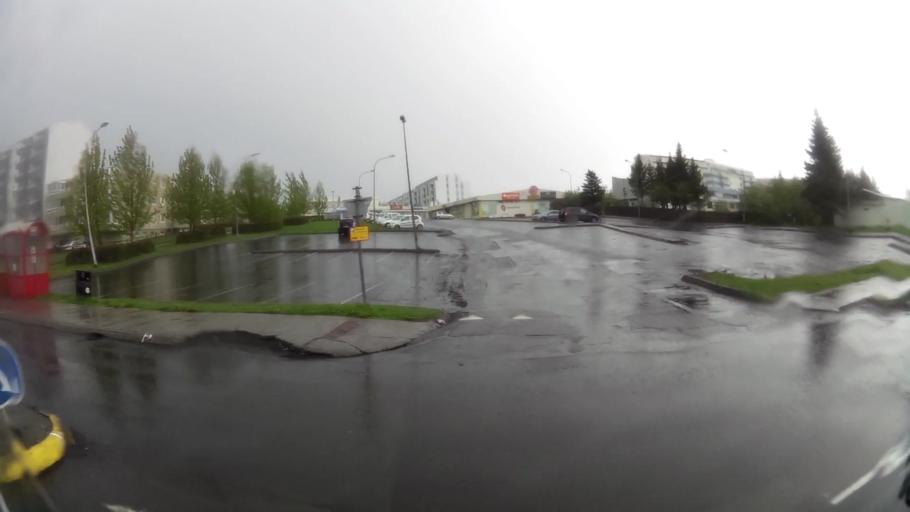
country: IS
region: Capital Region
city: Reykjavik
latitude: 64.1084
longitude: -21.8198
